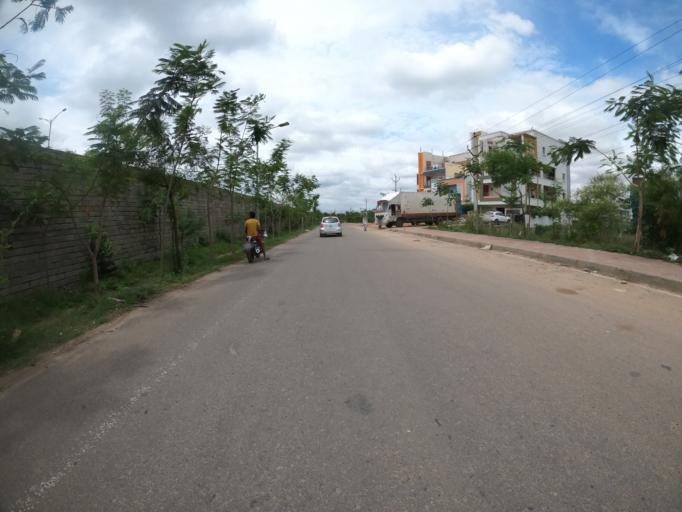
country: IN
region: Telangana
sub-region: Rangareddi
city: Sriramnagar
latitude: 17.2633
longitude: 78.3765
